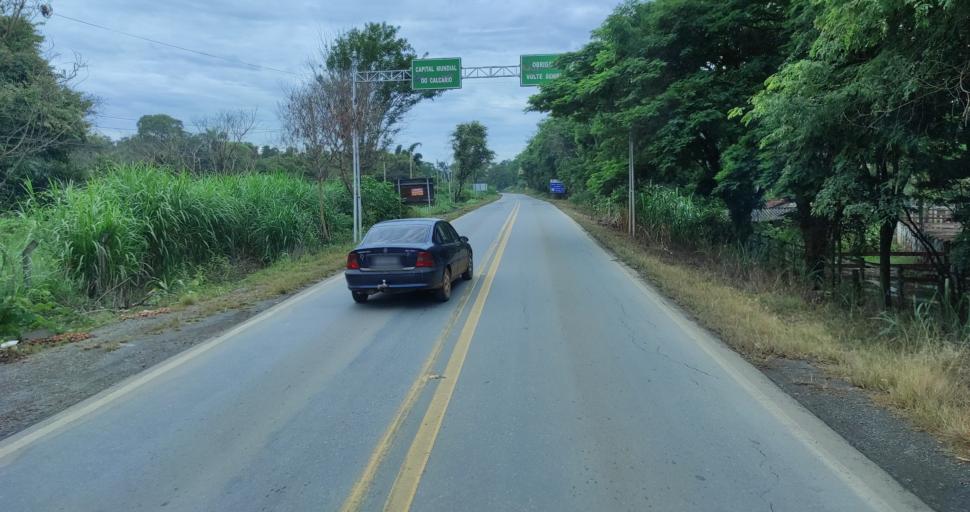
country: BR
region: Minas Gerais
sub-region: Arcos
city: Arcos
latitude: -20.3785
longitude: -45.6507
